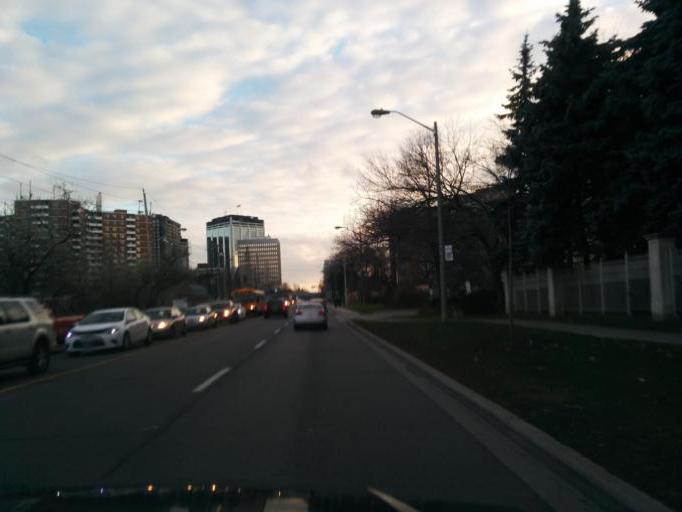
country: CA
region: Ontario
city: Etobicoke
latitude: 43.6500
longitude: -79.5258
